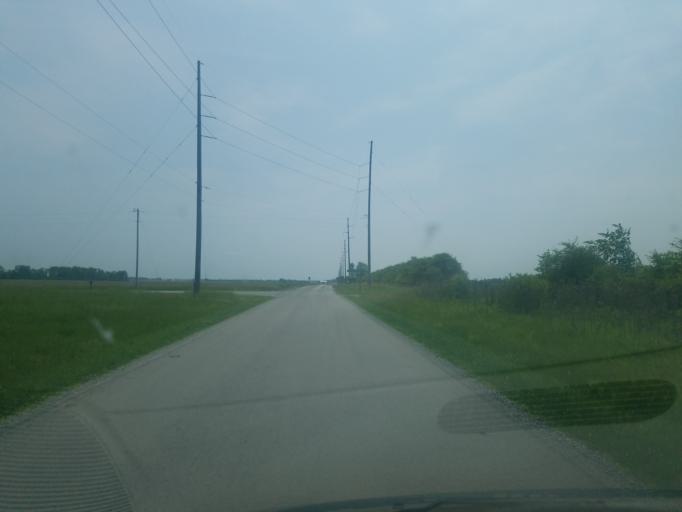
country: US
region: Ohio
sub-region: Wyandot County
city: Upper Sandusky
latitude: 40.7026
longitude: -83.2989
